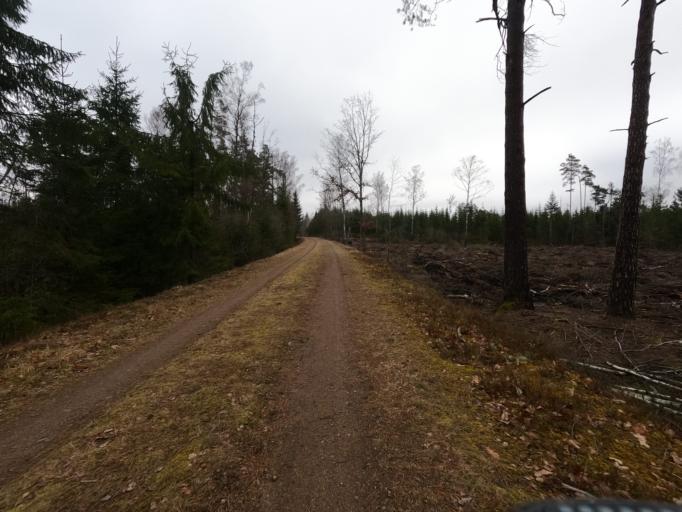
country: SE
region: Kronoberg
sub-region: Markaryds Kommun
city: Stromsnasbruk
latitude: 56.7883
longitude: 13.6607
